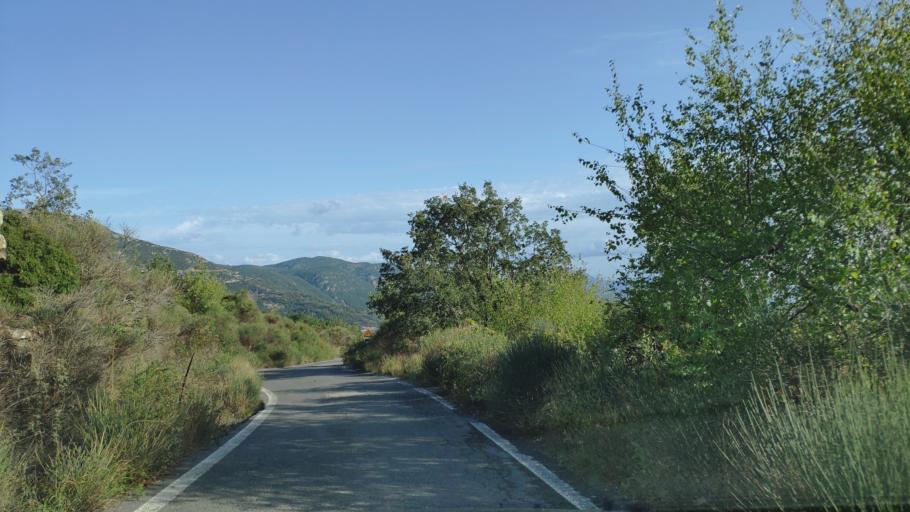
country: GR
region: Peloponnese
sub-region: Nomos Arkadias
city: Dimitsana
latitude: 37.5620
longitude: 22.0313
